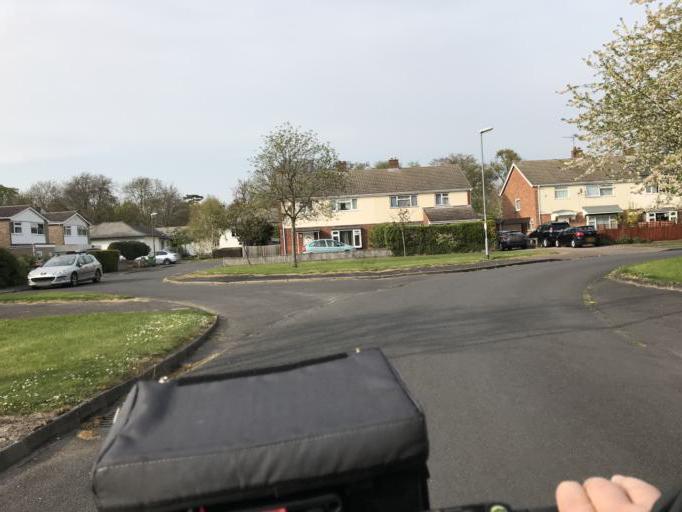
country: GB
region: England
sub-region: Cambridgeshire
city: Cambridge
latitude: 52.1838
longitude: 0.1655
